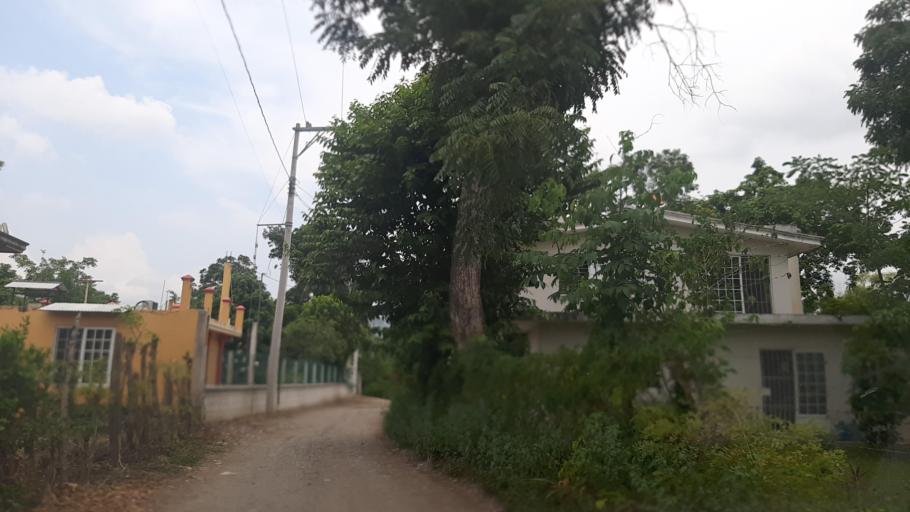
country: MX
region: Veracruz
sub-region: Tihuatlan
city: Ricardo Flores Magon
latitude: 20.5140
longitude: -97.4907
